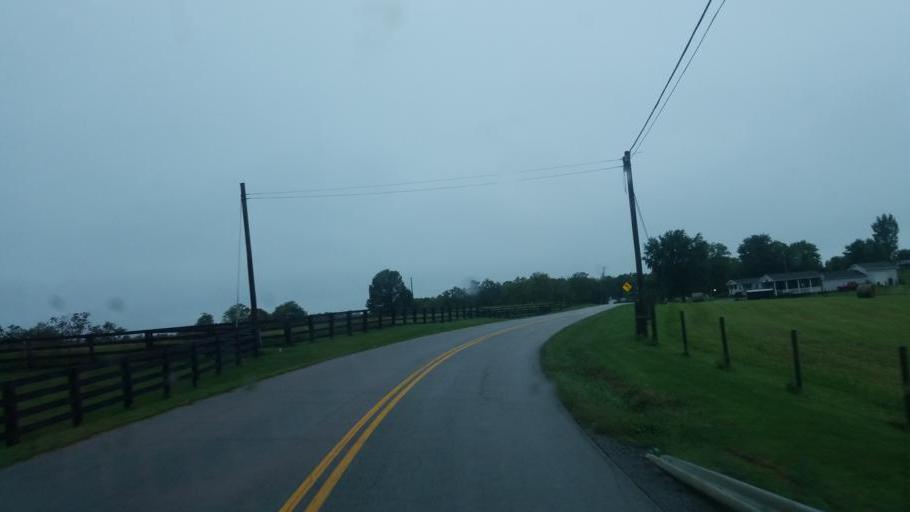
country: US
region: Kentucky
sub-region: Fleming County
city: Flemingsburg
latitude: 38.4257
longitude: -83.7183
